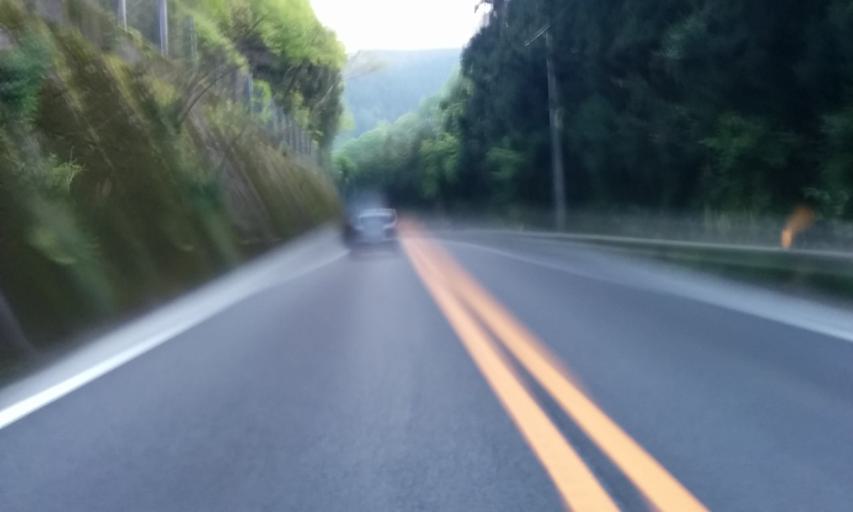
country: JP
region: Ehime
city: Saijo
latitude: 33.8350
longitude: 132.9906
